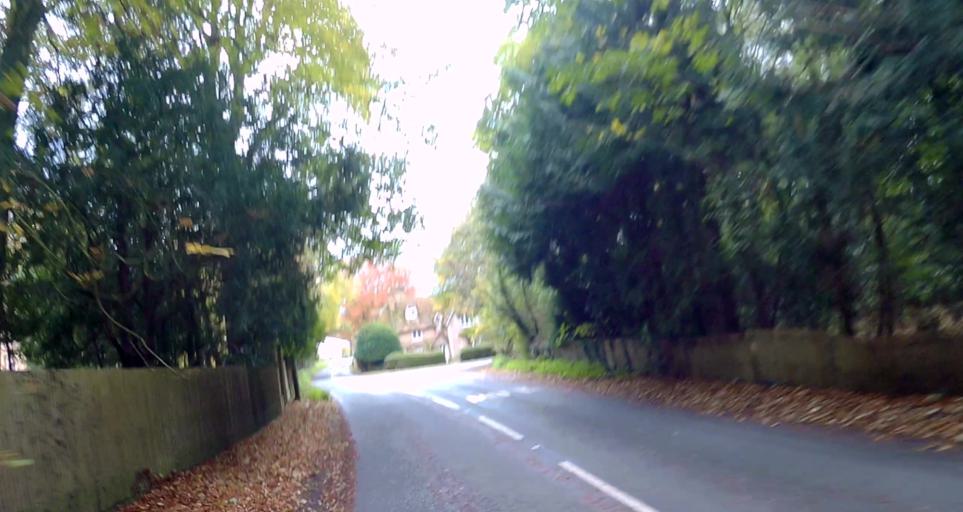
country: GB
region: England
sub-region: Hampshire
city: Basingstoke
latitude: 51.1690
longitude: -1.1366
